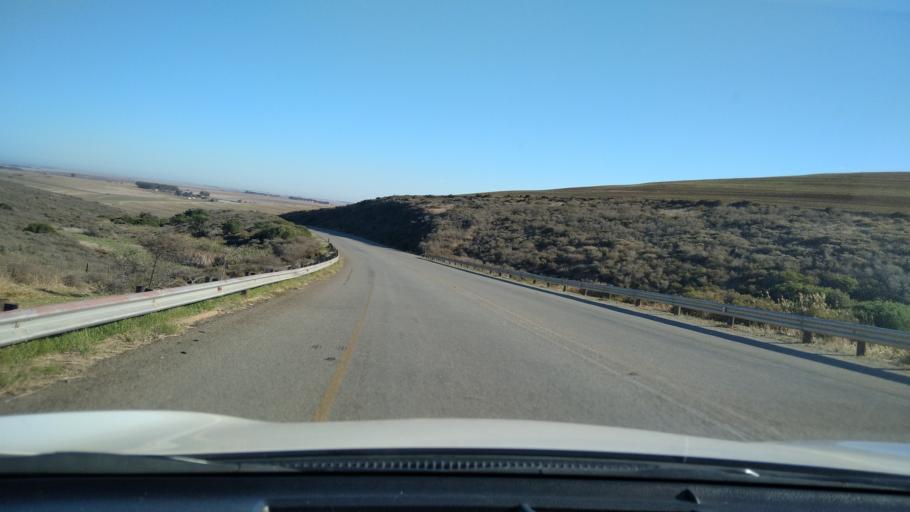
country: ZA
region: Western Cape
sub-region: West Coast District Municipality
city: Malmesbury
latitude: -33.3835
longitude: 18.6698
